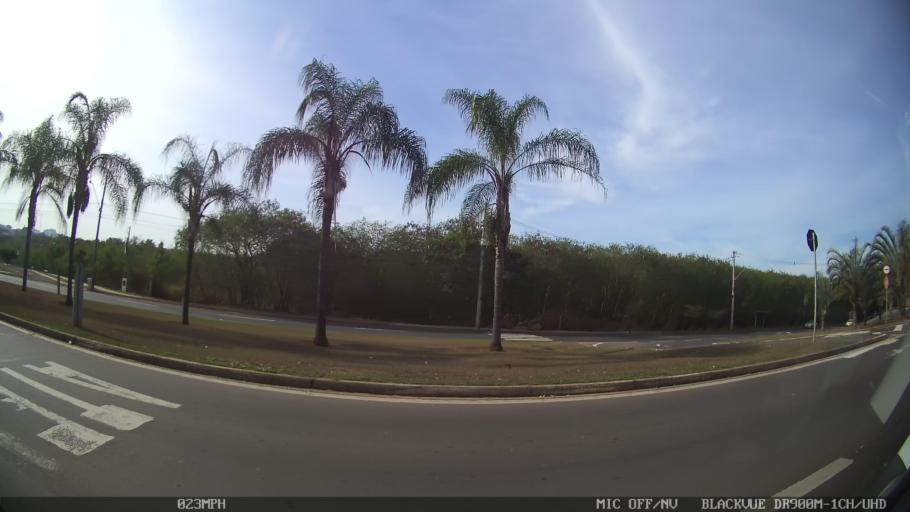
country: BR
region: Sao Paulo
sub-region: Piracicaba
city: Piracicaba
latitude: -22.7040
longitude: -47.6764
